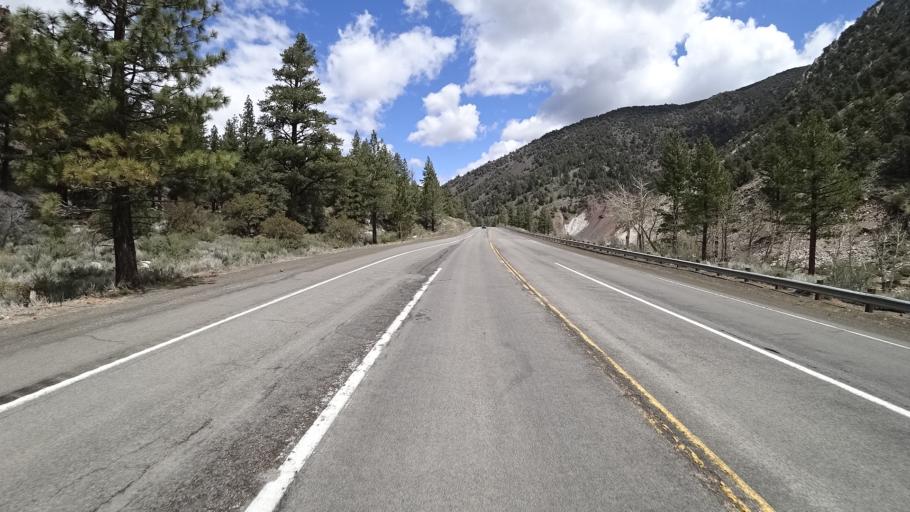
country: US
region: California
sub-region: Mono County
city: Bridgeport
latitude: 38.4168
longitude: -119.4499
